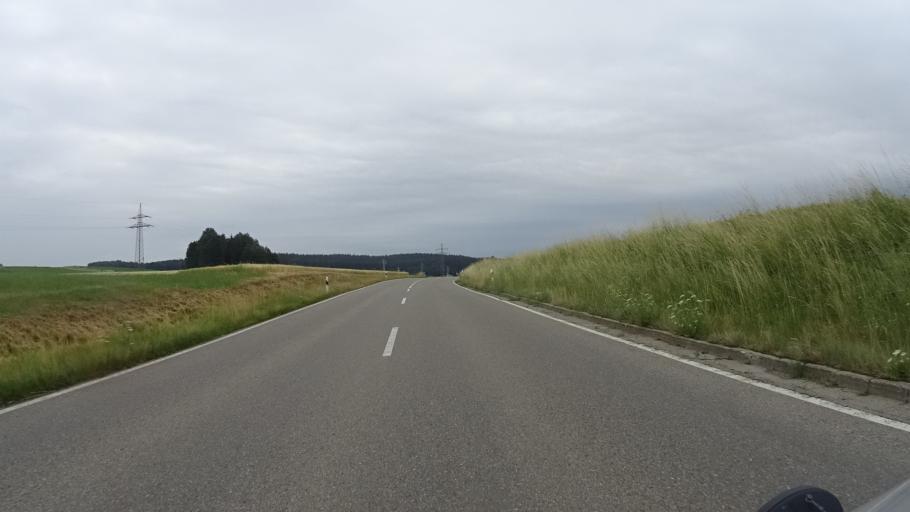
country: DE
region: Bavaria
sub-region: Swabia
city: Kellmunz
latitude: 48.1177
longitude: 10.1384
